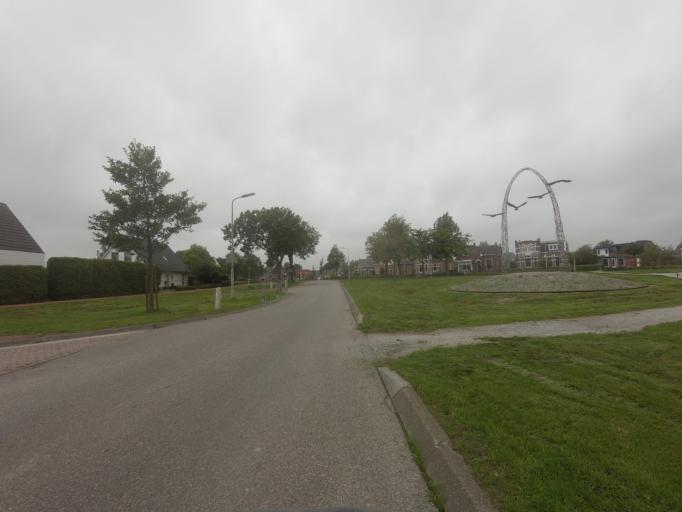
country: NL
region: Friesland
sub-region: Gemeente Ferwerderadiel
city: Ferwert
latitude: 53.3362
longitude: 5.8279
